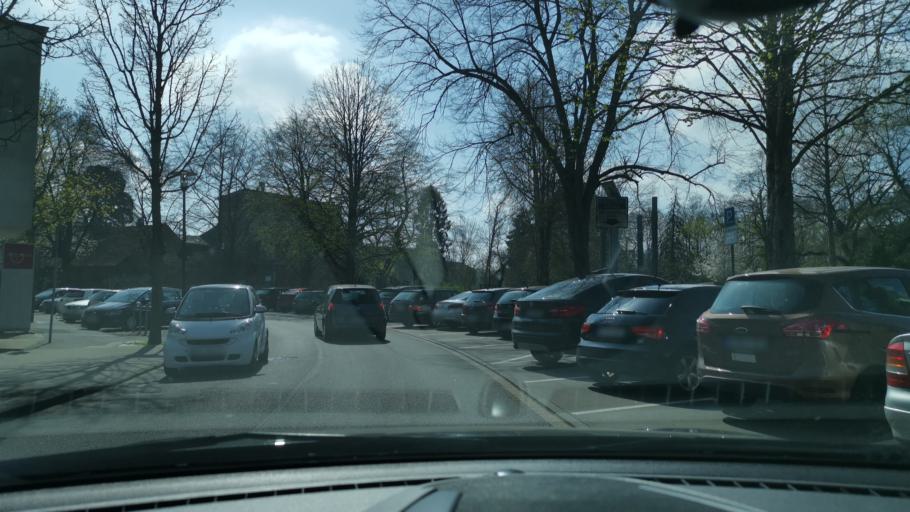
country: DE
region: North Rhine-Westphalia
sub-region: Regierungsbezirk Dusseldorf
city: Grevenbroich
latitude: 51.0883
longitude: 6.5877
